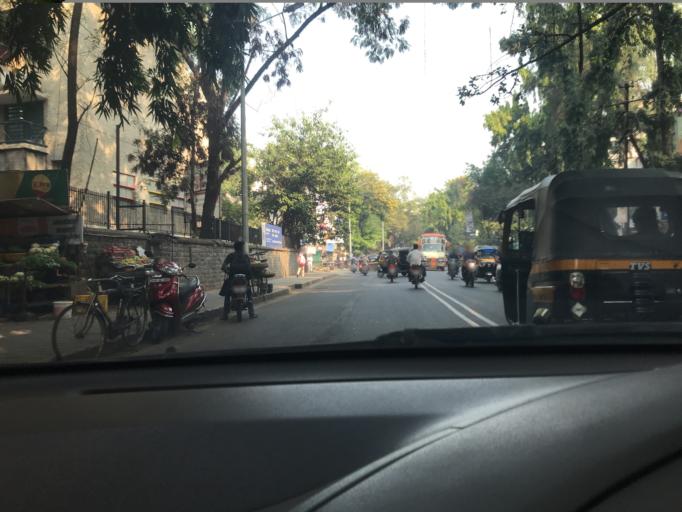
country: IN
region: Maharashtra
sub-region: Pune Division
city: Pune
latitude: 18.5139
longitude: 73.8288
